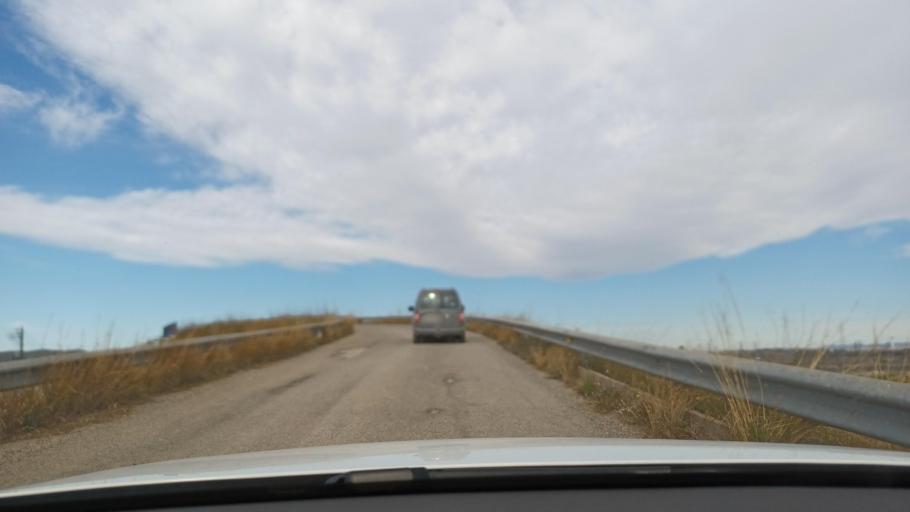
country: ES
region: Valencia
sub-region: Provincia de Valencia
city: Benifaio
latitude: 39.2910
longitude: -0.4358
